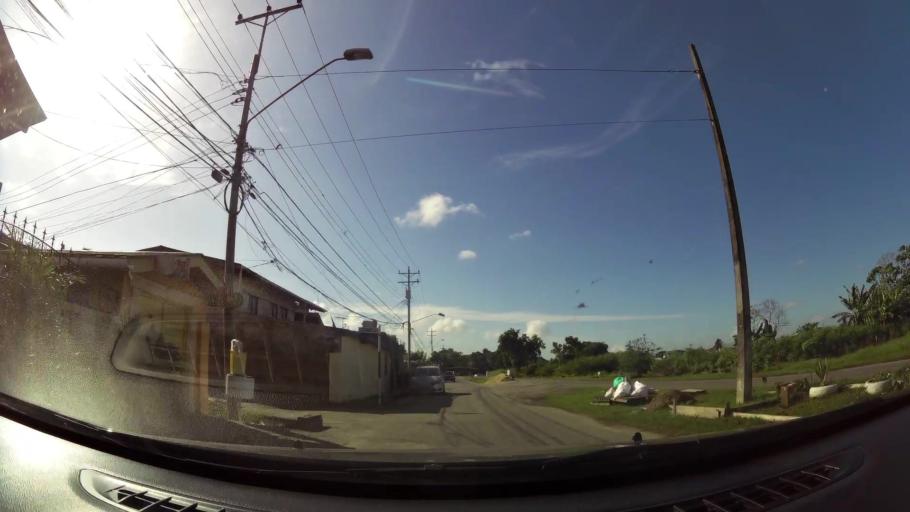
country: TT
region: Chaguanas
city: Chaguanas
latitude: 10.5275
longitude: -61.3962
